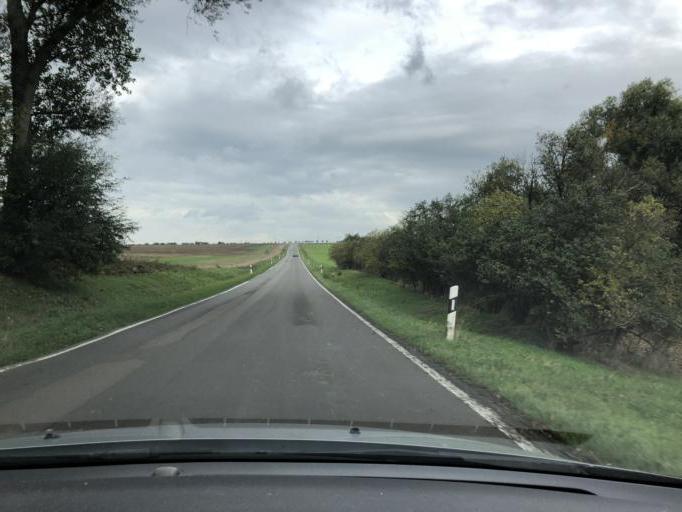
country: DE
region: Saxony-Anhalt
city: Uichteritz
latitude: 51.2119
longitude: 11.8958
